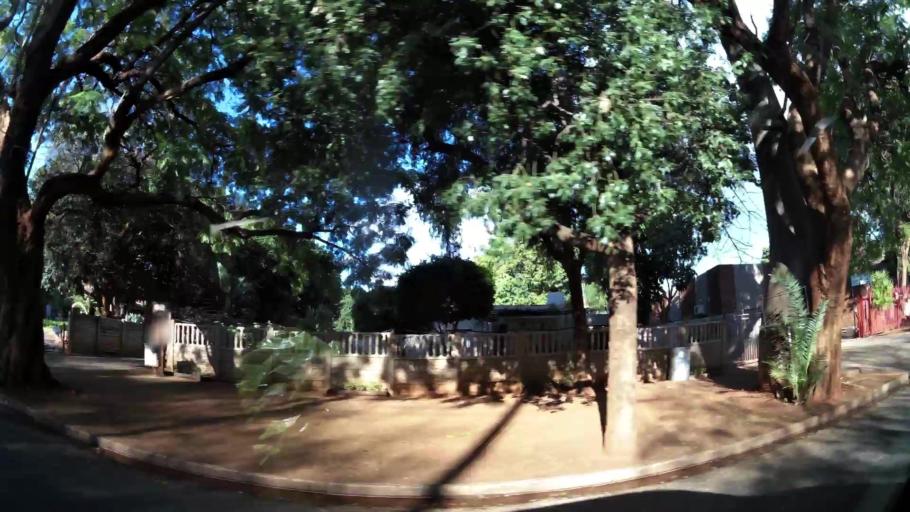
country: ZA
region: Limpopo
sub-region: Waterberg District Municipality
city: Mokopane
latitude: -24.1866
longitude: 28.9984
